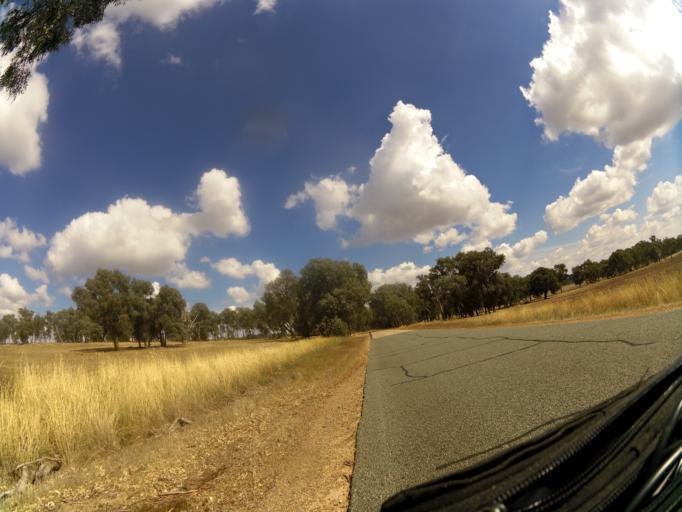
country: AU
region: Victoria
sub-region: Benalla
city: Benalla
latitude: -36.7245
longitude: 146.0836
